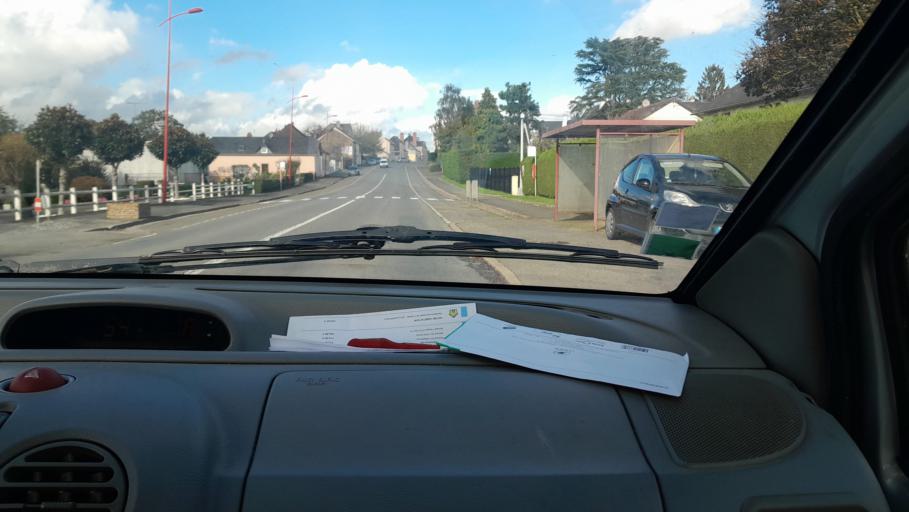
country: FR
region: Pays de la Loire
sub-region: Departement de la Mayenne
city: Cosse-le-Vivien
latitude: 47.9406
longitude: -0.9144
